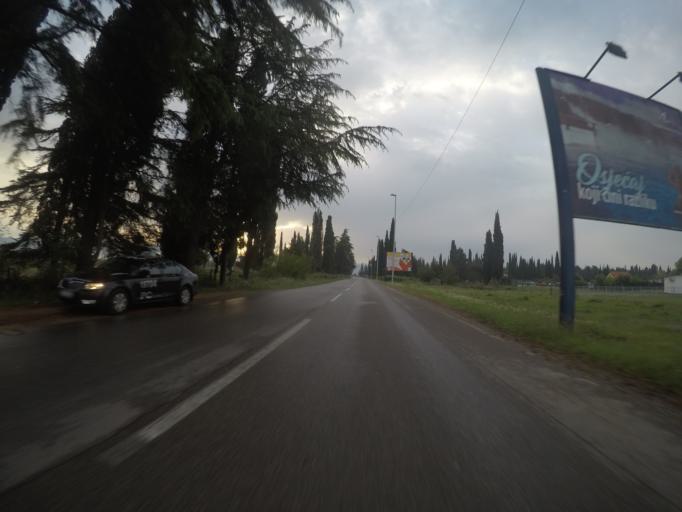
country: ME
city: Mojanovici
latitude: 42.3651
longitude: 19.2394
